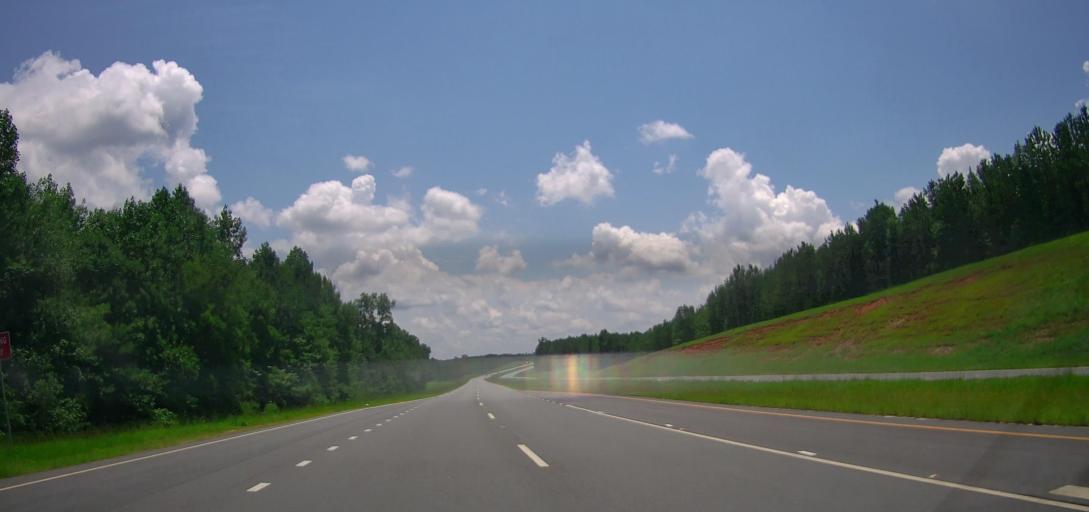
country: US
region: Georgia
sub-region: Upson County
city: Thomaston
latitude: 32.7881
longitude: -84.2486
